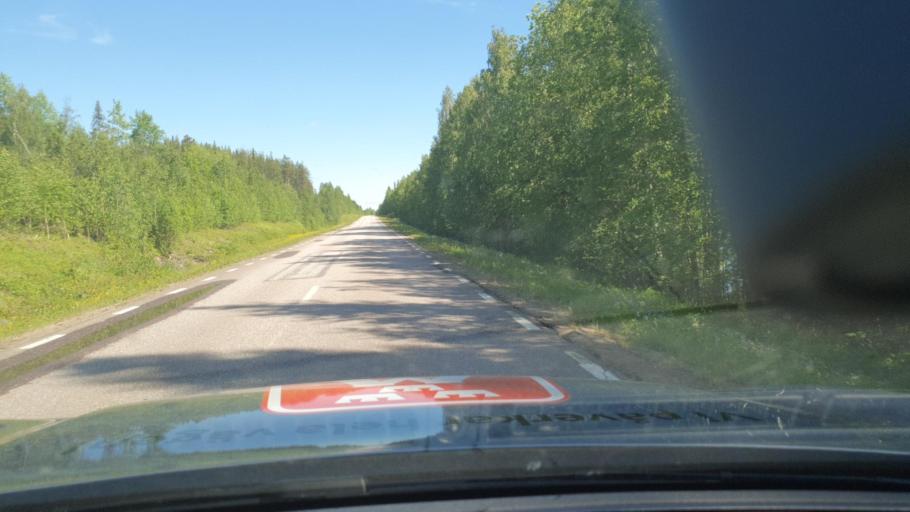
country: SE
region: Norrbotten
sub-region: Overkalix Kommun
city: OEverkalix
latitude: 66.7953
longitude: 22.7265
